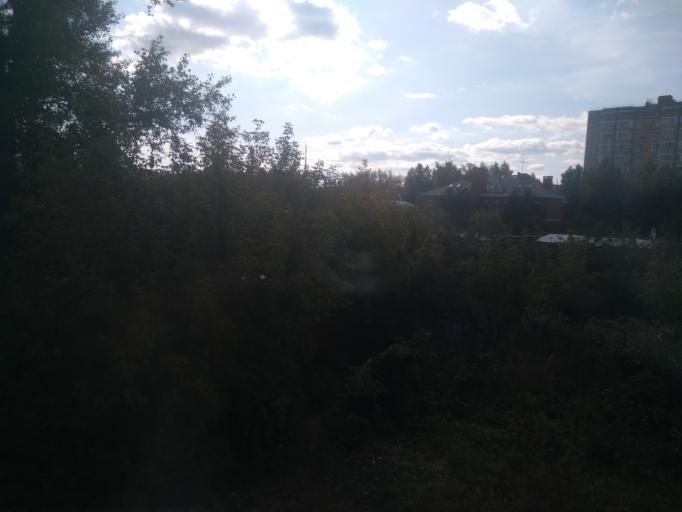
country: RU
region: Tatarstan
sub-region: Gorod Kazan'
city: Kazan
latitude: 55.8031
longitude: 49.0628
